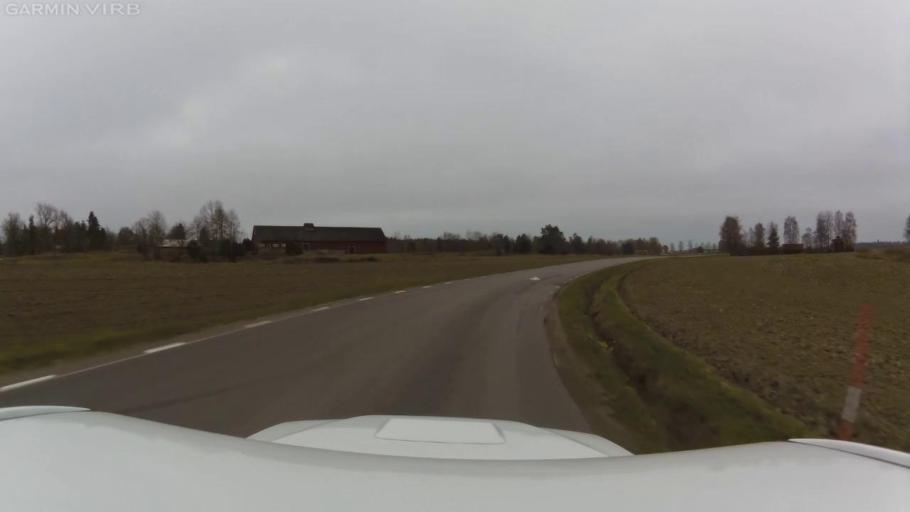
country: SE
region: OEstergoetland
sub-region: Linkopings Kommun
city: Vikingstad
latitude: 58.3669
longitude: 15.4313
